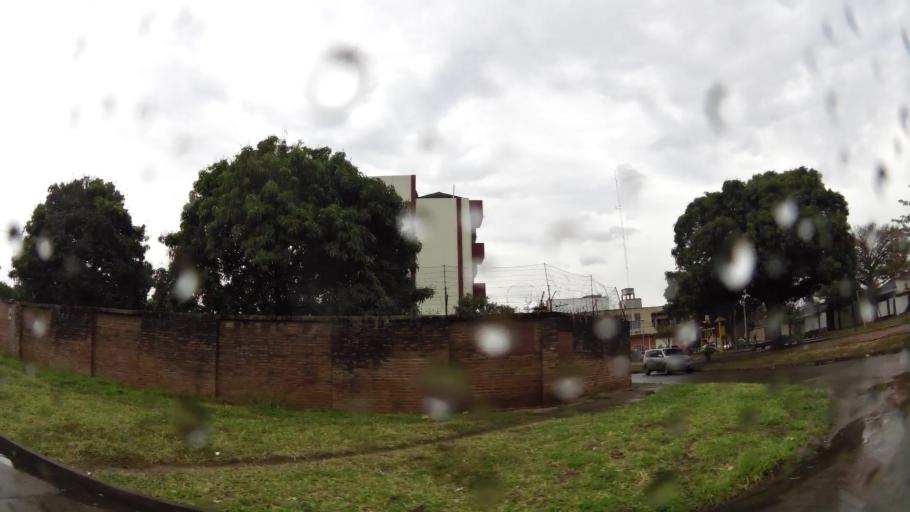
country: BO
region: Santa Cruz
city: Santa Cruz de la Sierra
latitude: -17.7640
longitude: -63.1511
